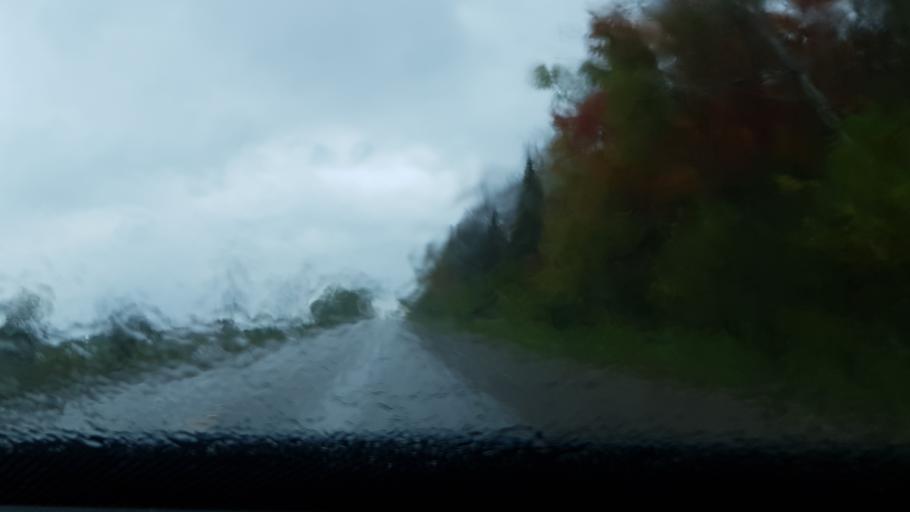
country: CA
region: Ontario
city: Omemee
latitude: 44.3928
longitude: -78.5635
